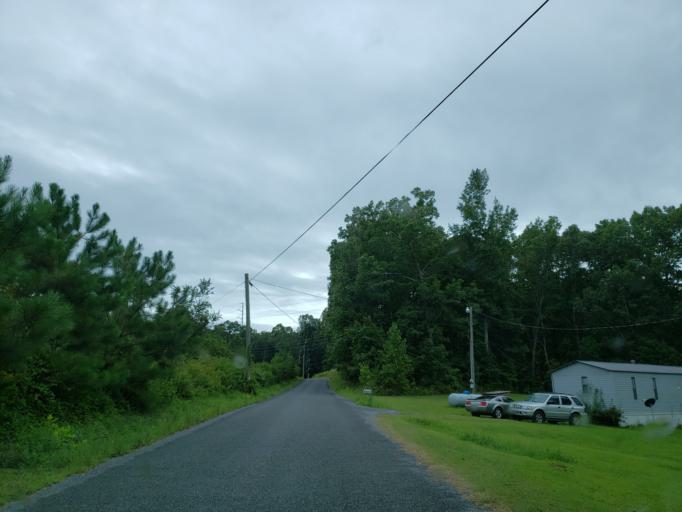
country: US
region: Georgia
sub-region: Gilmer County
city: Ellijay
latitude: 34.6221
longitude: -84.5782
